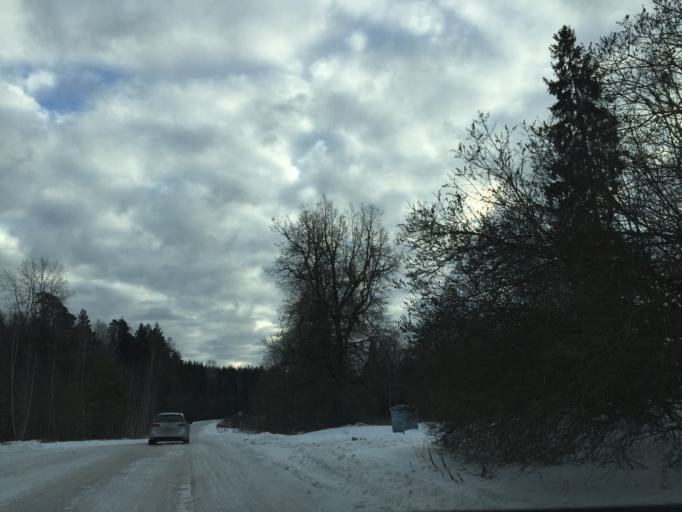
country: LV
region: Lielvarde
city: Lielvarde
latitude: 56.6247
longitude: 24.7719
